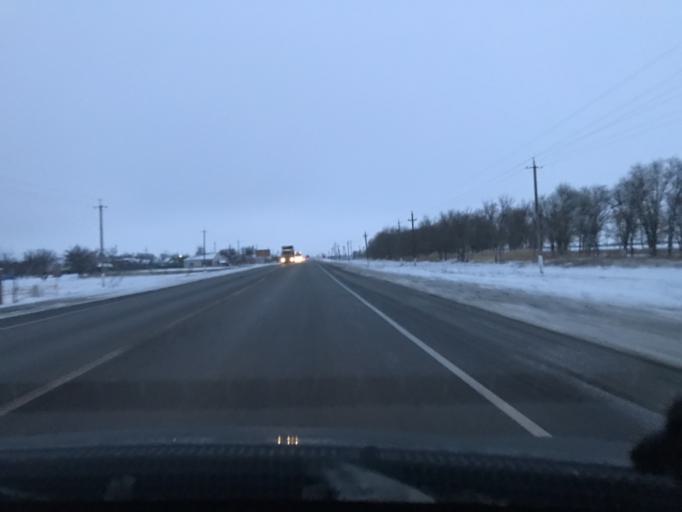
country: RU
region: Rostov
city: Letnik
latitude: 45.9044
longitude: 41.2977
